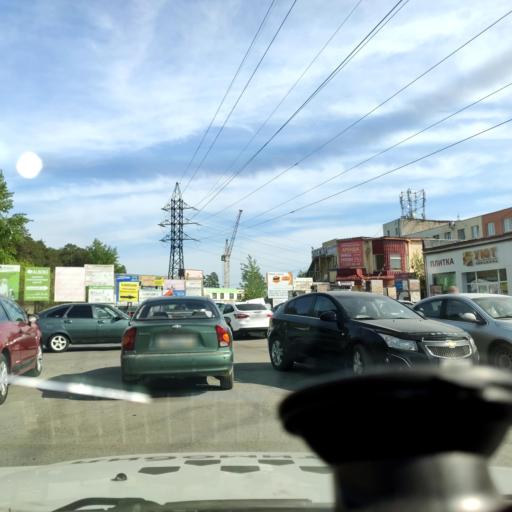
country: RU
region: Sverdlovsk
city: Sovkhoznyy
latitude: 56.7773
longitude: 60.5652
